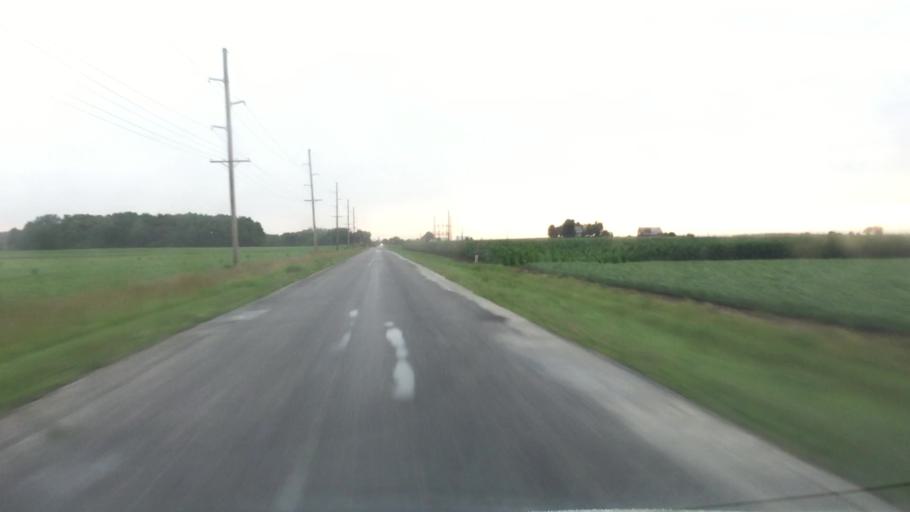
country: US
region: Iowa
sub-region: Lee County
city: Fort Madison
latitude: 40.5613
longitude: -91.2686
